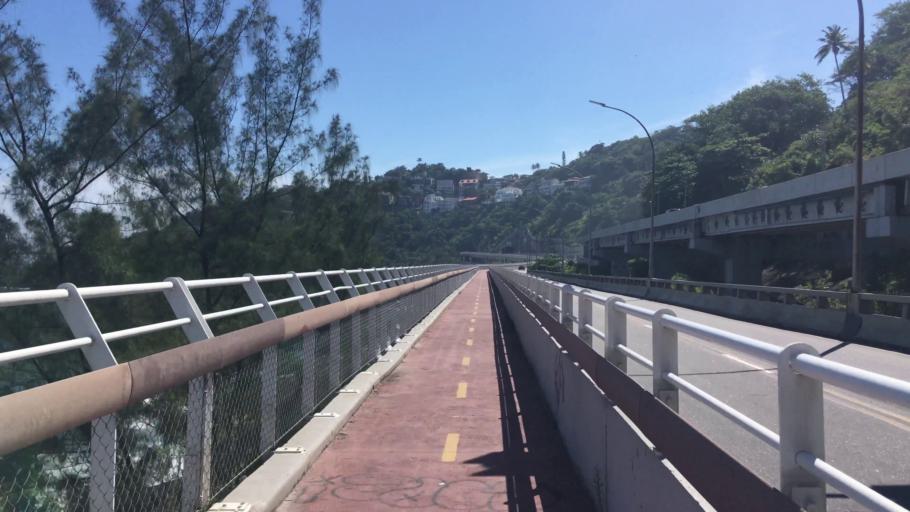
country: BR
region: Rio de Janeiro
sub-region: Rio De Janeiro
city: Rio de Janeiro
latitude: -23.0068
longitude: -43.2827
